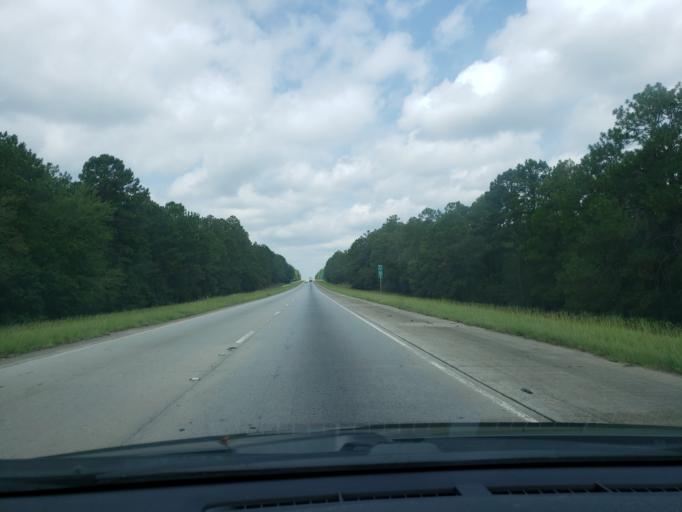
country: US
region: Georgia
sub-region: Emanuel County
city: Swainsboro
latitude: 32.4135
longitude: -82.3712
